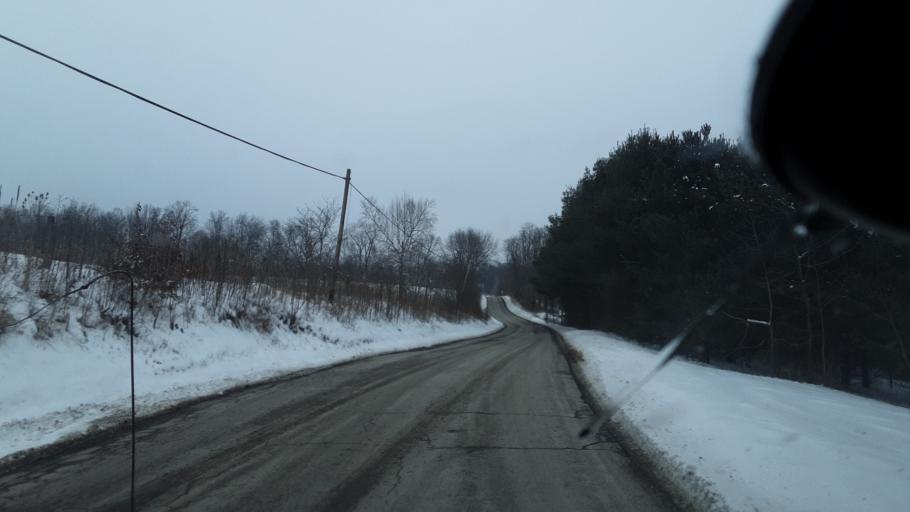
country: US
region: Ohio
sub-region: Muskingum County
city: Zanesville
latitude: 39.9412
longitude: -82.1769
